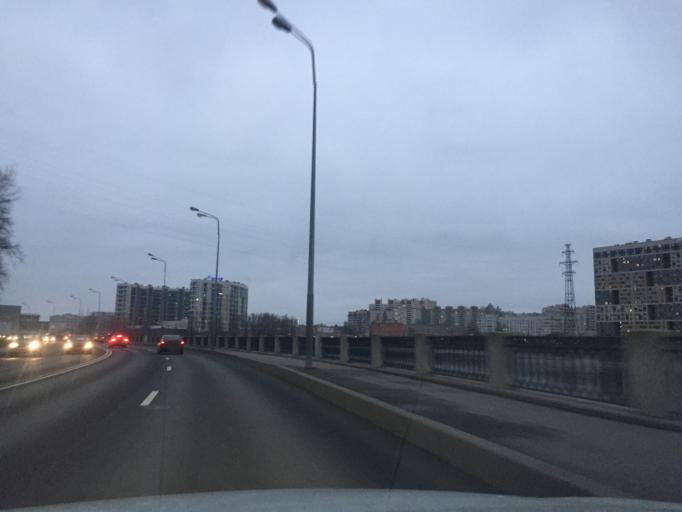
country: RU
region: St.-Petersburg
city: Obukhovo
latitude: 59.8732
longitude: 30.4610
